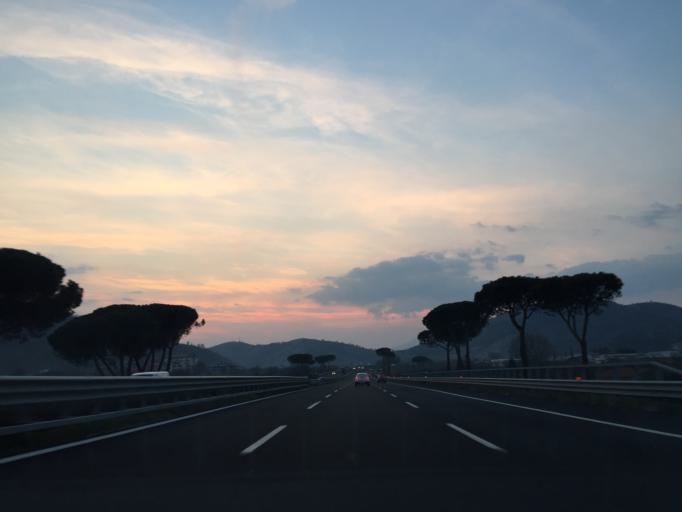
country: IT
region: Campania
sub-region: Provincia di Salerno
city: Casali-San Potito
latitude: 40.7670
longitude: 14.6831
